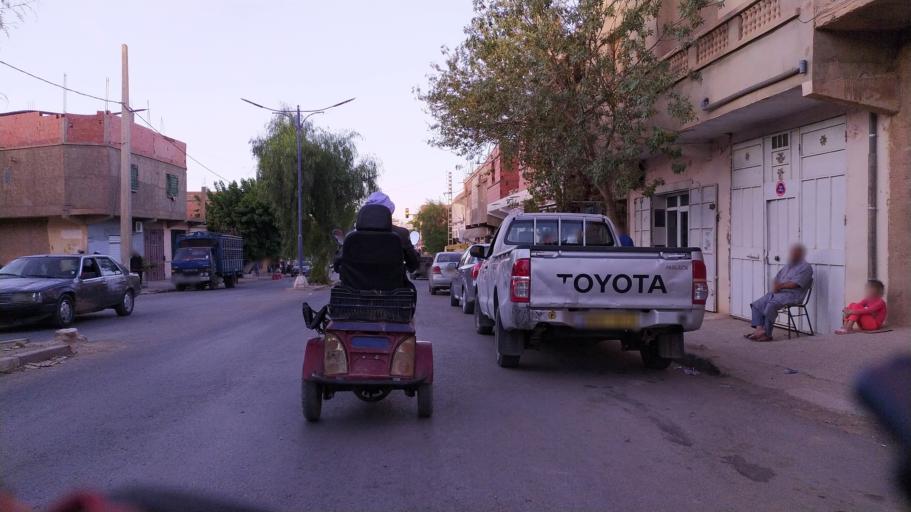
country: DZ
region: Tiaret
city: Frenda
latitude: 34.8934
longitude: 1.2468
